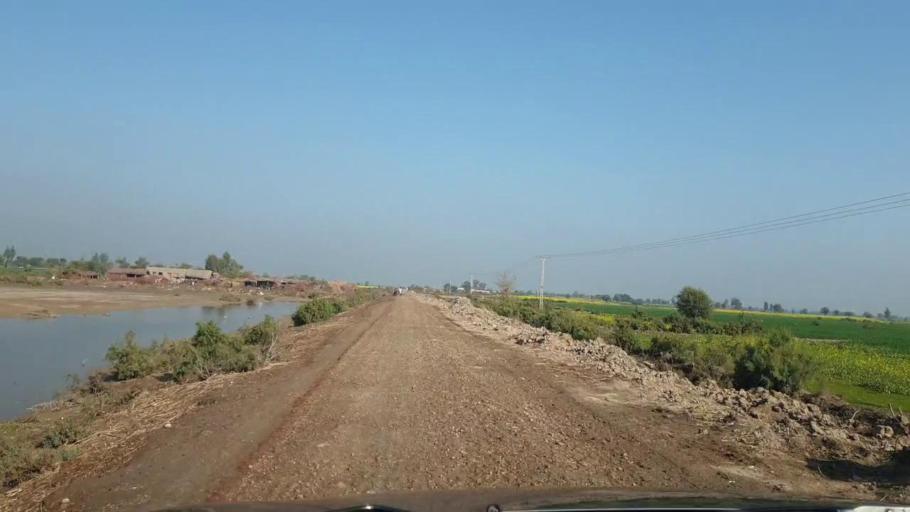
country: PK
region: Sindh
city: Sinjhoro
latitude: 26.0379
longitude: 68.7889
